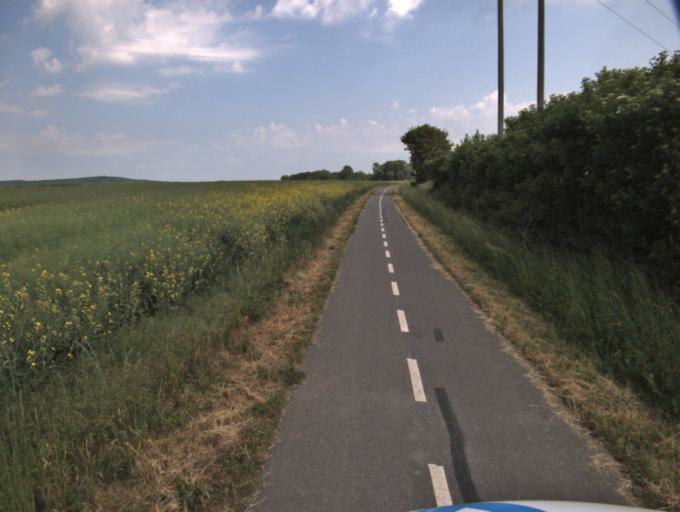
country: SE
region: Skane
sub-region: Kristianstads Kommun
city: Kristianstad
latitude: 56.0690
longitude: 14.1954
